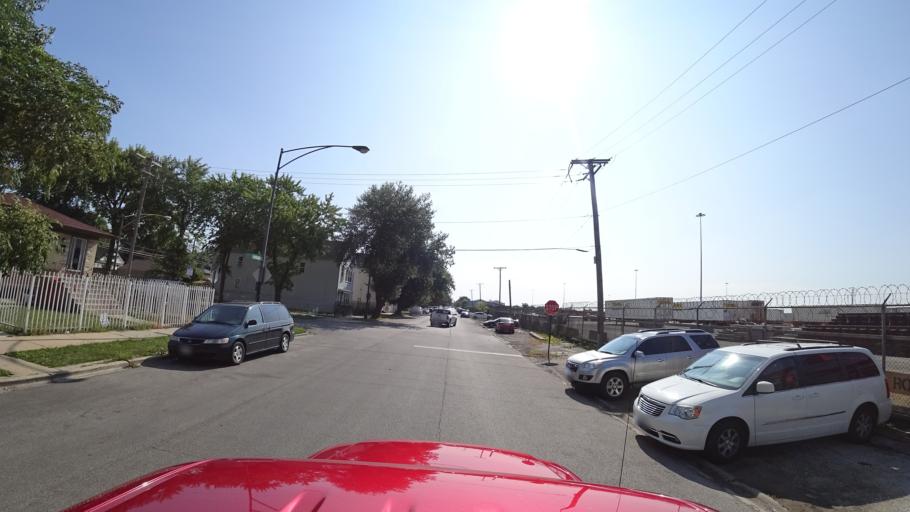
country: US
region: Illinois
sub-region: Cook County
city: Cicero
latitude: 41.8225
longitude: -87.7121
